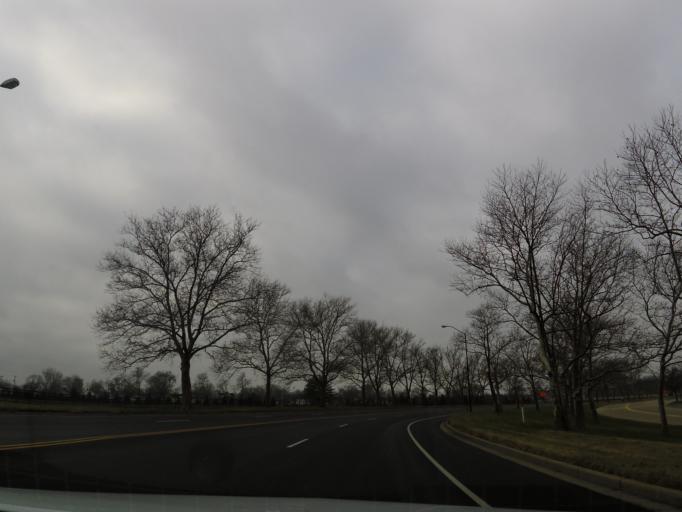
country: US
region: Indiana
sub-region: Bartholomew County
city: Columbus
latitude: 39.2026
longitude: -85.9053
